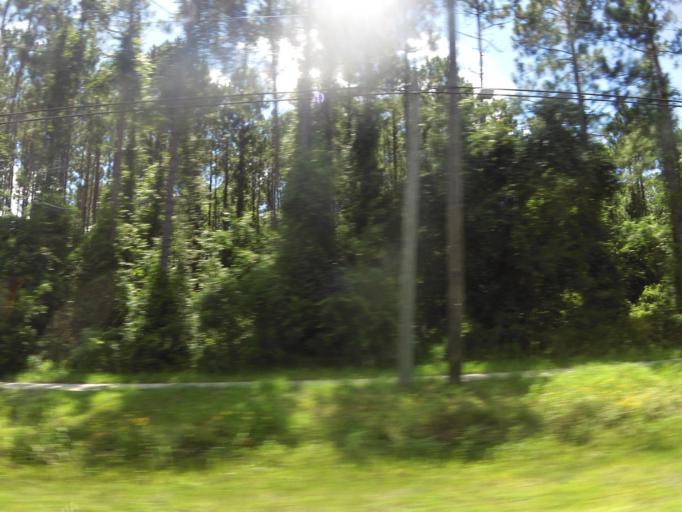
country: US
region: Florida
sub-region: Nassau County
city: Fernandina Beach
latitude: 30.6479
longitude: -81.5302
